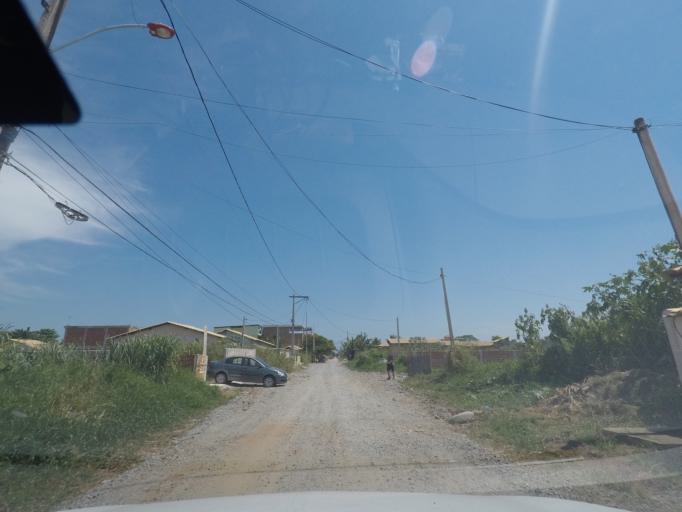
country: BR
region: Rio de Janeiro
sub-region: Marica
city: Marica
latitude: -22.9526
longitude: -42.9568
